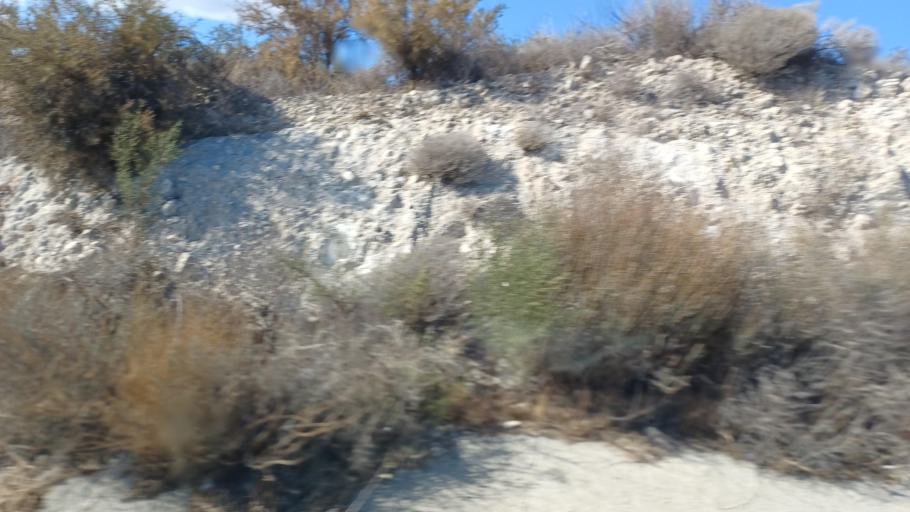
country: CY
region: Limassol
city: Pyrgos
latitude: 34.7608
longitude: 33.2289
